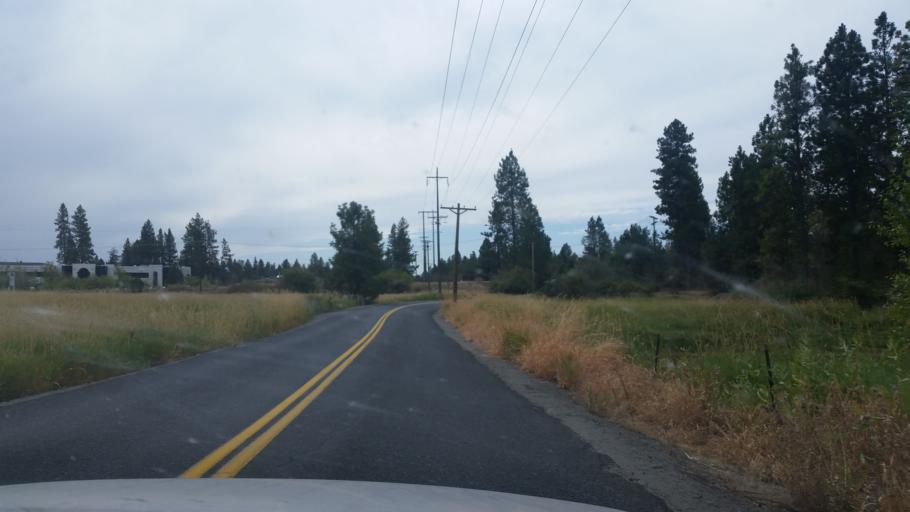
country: US
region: Washington
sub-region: Spokane County
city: Spokane
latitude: 47.6449
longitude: -117.4968
